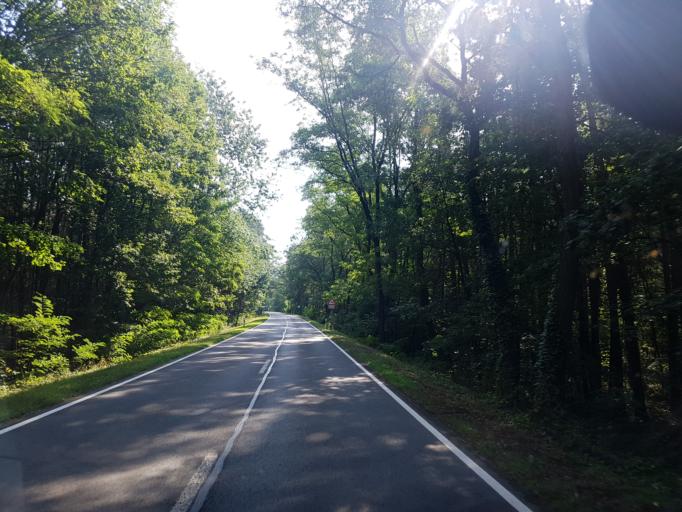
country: DE
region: Brandenburg
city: Lauchhammer
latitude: 51.5307
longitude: 13.6853
